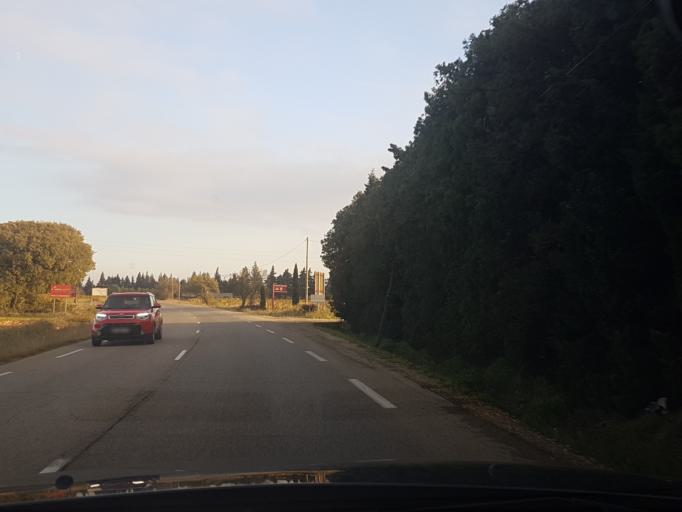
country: FR
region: Provence-Alpes-Cote d'Azur
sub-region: Departement du Vaucluse
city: Sorgues
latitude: 44.0327
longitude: 4.8591
